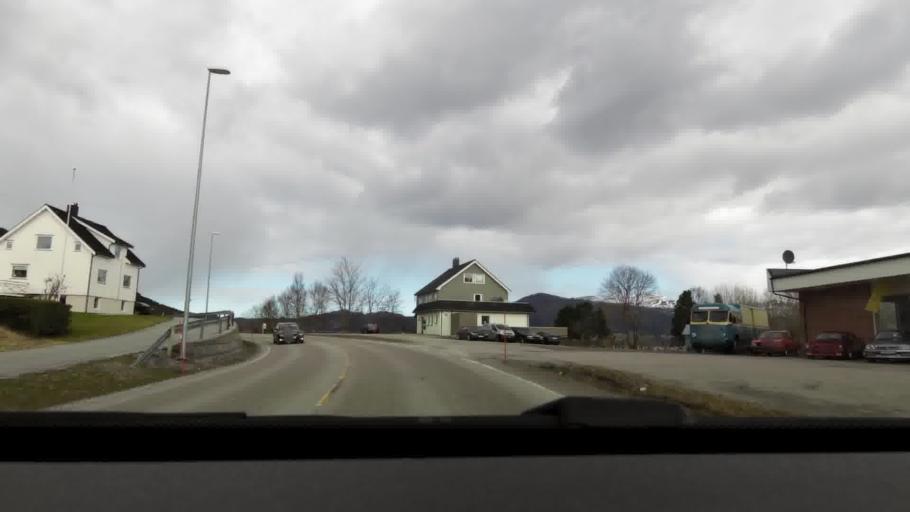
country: NO
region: More og Romsdal
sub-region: Eide
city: Eide
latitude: 62.9208
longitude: 7.4507
